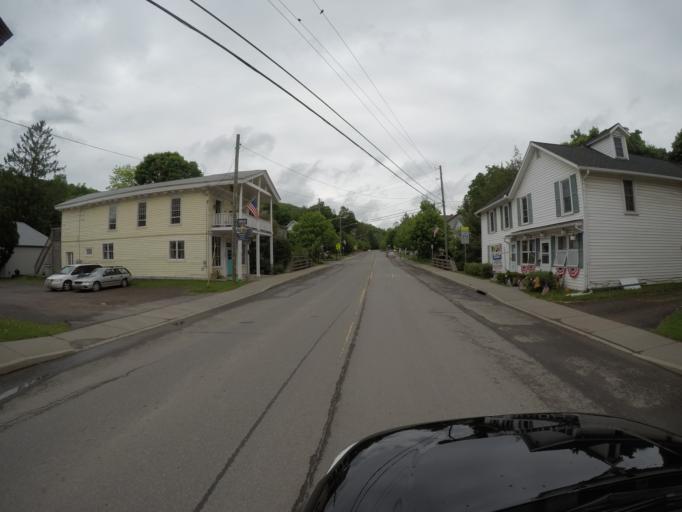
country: US
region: New York
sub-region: Delaware County
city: Delhi
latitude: 42.1891
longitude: -74.7859
